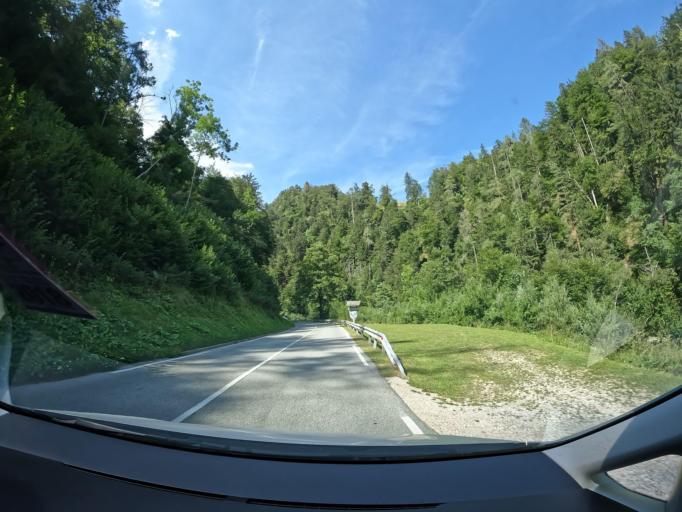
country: SI
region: Trzic
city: Trzic
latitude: 46.3887
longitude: 14.3589
